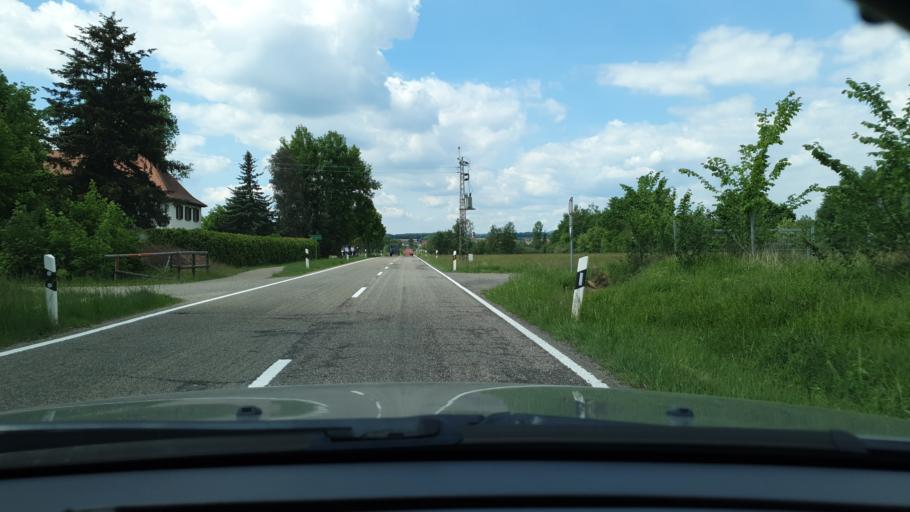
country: DE
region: Rheinland-Pfalz
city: Hauptstuhl
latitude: 49.4067
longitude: 7.4905
